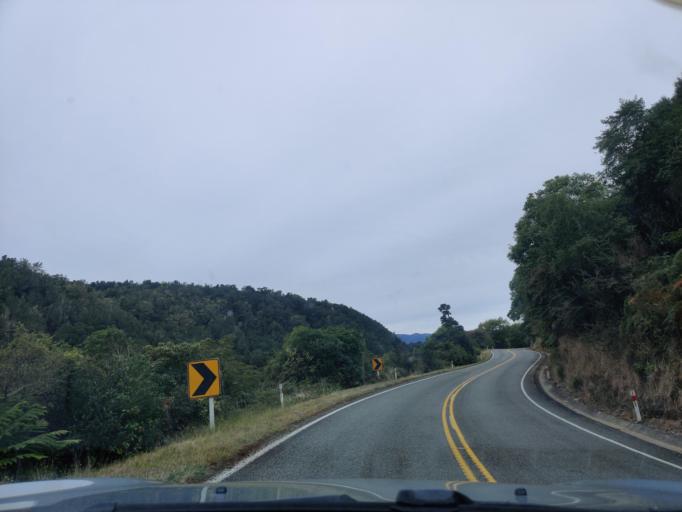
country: NZ
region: West Coast
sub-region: Buller District
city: Westport
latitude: -41.8368
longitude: 171.9275
